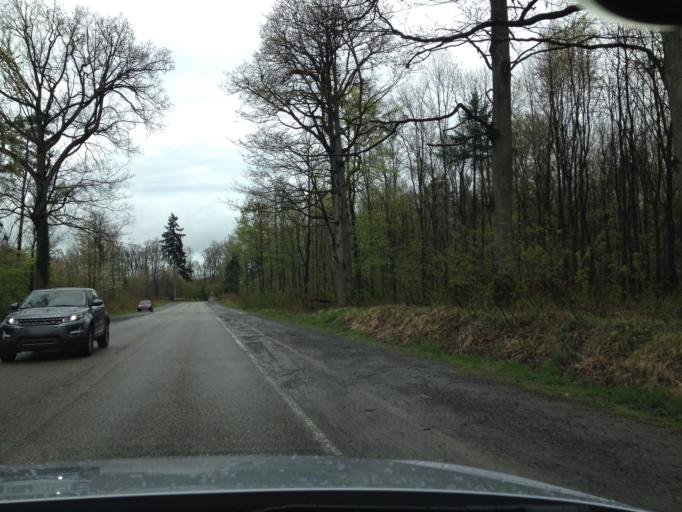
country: DE
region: Baden-Wuerttemberg
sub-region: Regierungsbezirk Stuttgart
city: Weinsberg
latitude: 49.1279
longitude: 9.2691
